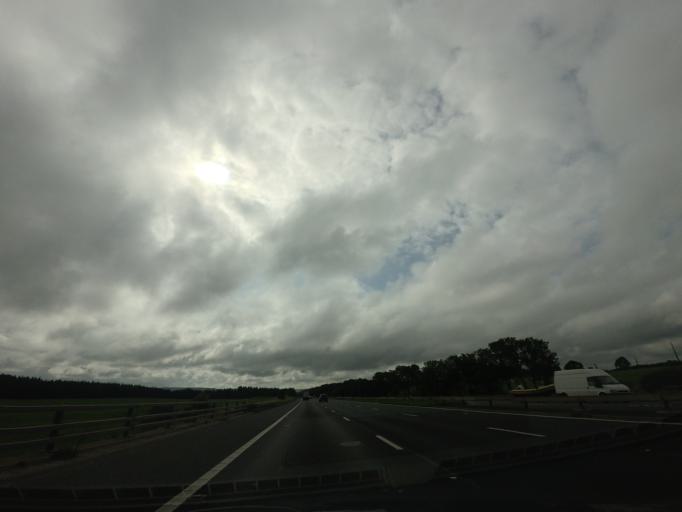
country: GB
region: England
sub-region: Cumbria
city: Scotby
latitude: 54.7669
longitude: -2.8392
